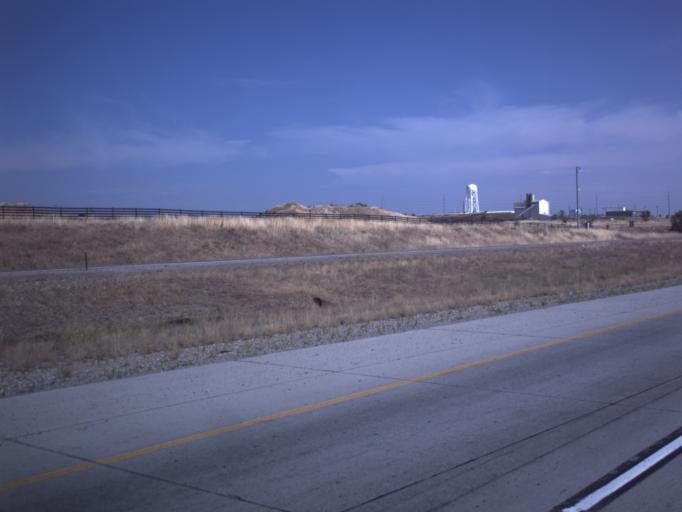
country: US
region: Utah
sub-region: Salt Lake County
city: Oquirrh
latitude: 40.6443
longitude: -112.0448
